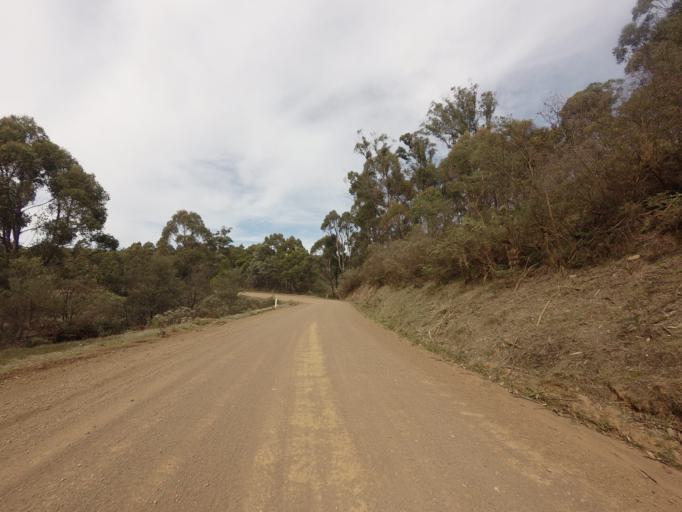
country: AU
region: Tasmania
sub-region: Sorell
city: Sorell
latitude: -42.4991
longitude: 147.6310
